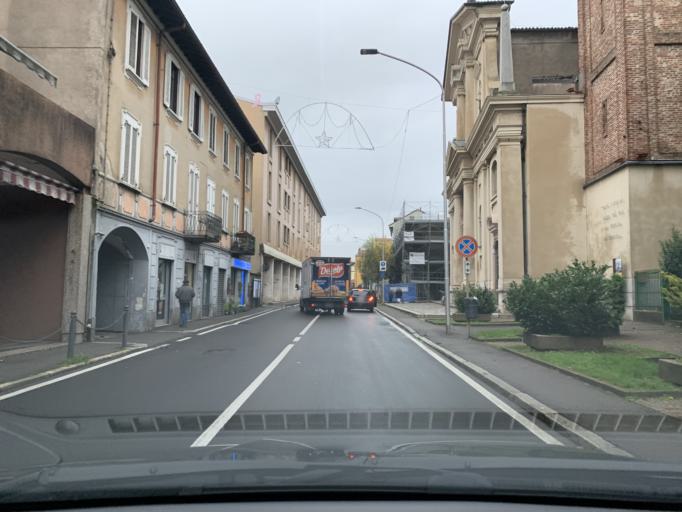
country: IT
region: Lombardy
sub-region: Provincia di Como
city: Rovellasca
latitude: 45.6670
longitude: 9.0546
